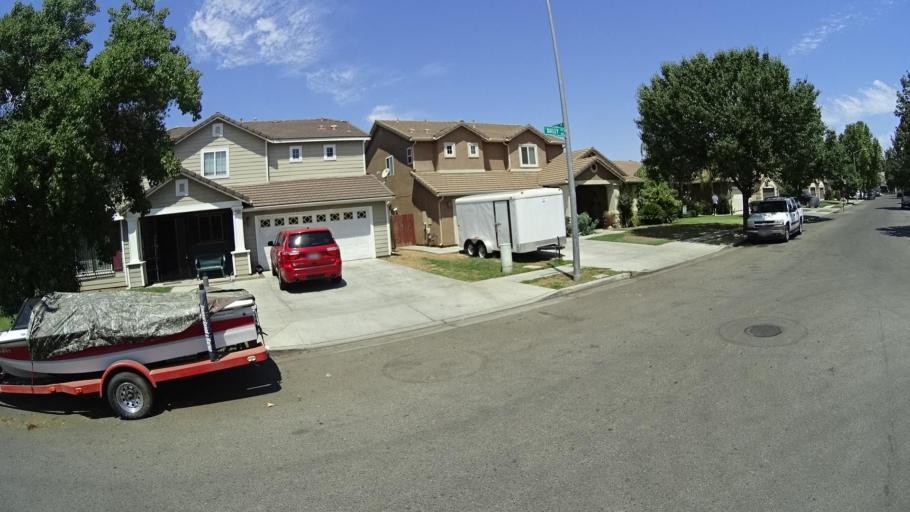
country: US
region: California
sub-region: Fresno County
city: Sunnyside
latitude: 36.7302
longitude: -119.7211
